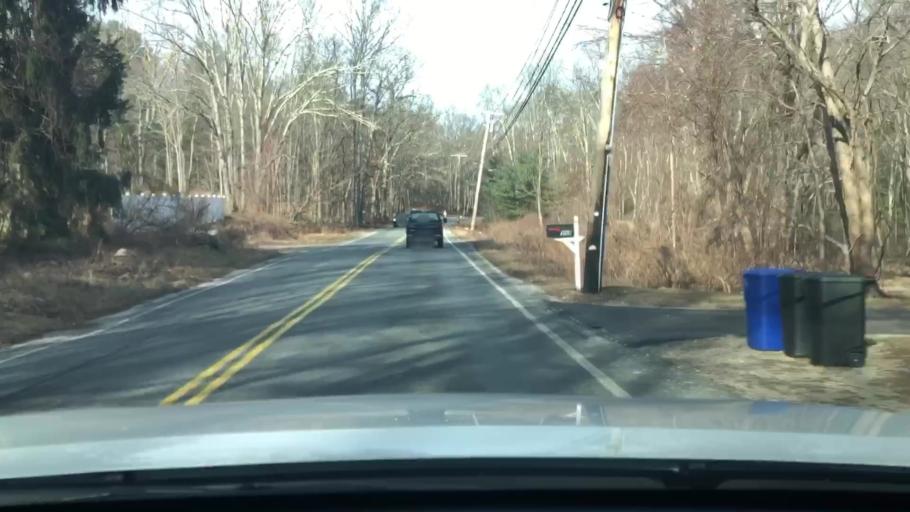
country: US
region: Massachusetts
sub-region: Worcester County
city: Mendon
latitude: 42.0791
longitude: -71.5285
